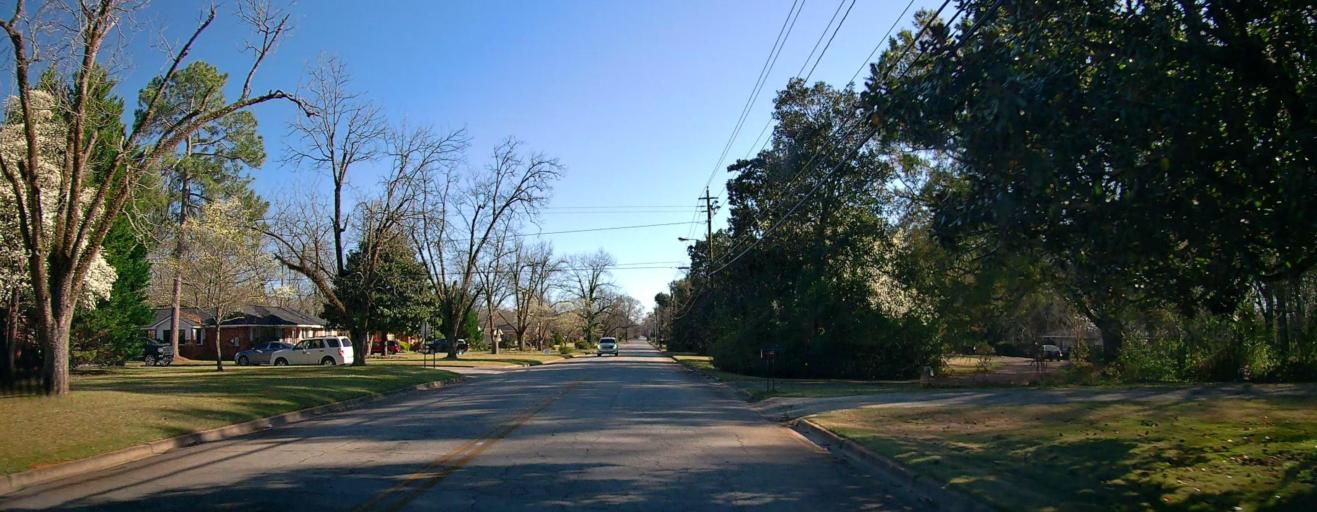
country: US
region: Georgia
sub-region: Peach County
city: Fort Valley
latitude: 32.5701
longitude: -83.8932
